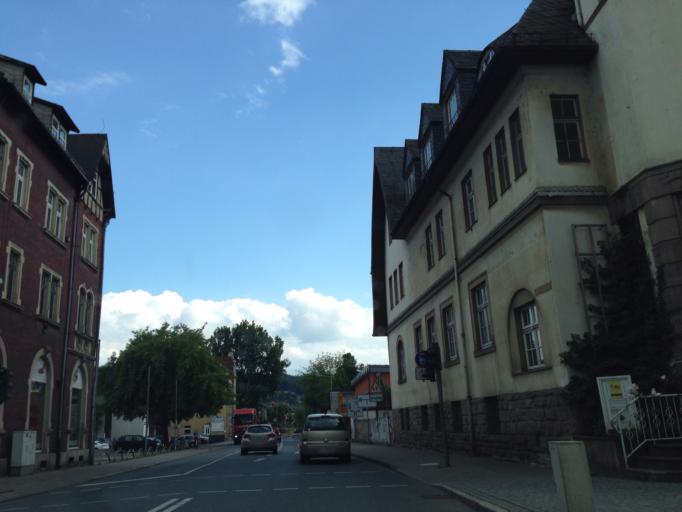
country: DE
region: Thuringia
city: Rudolstadt
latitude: 50.7209
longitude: 11.3442
